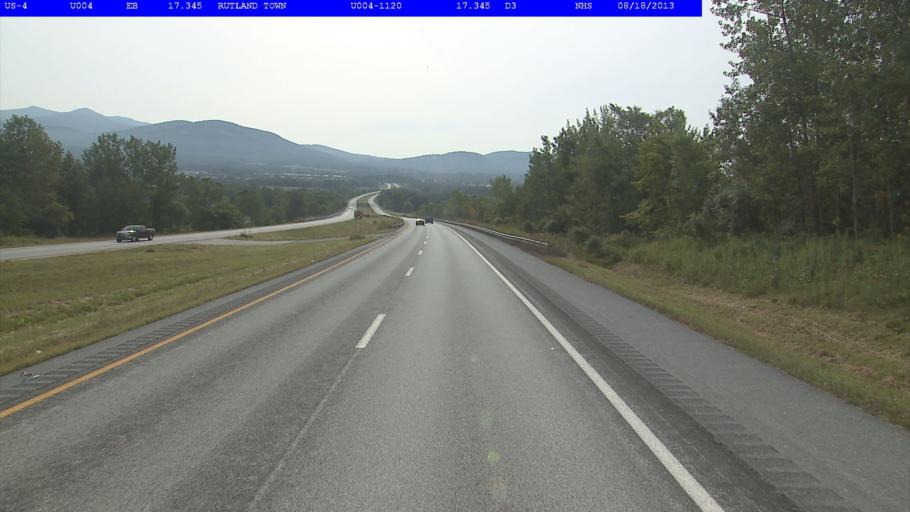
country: US
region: Vermont
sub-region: Rutland County
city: Rutland
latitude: 43.5862
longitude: -72.9941
